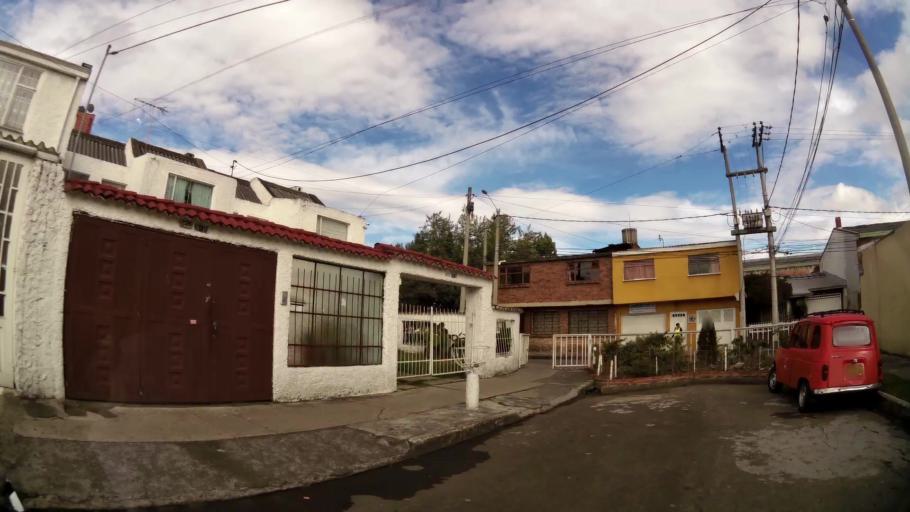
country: CO
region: Bogota D.C.
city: Barrio San Luis
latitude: 4.6968
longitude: -74.0776
